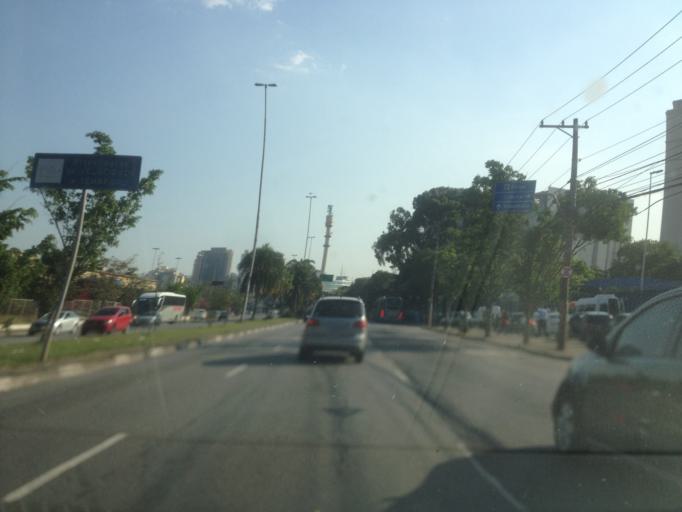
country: BR
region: Sao Paulo
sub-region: Sao Paulo
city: Sao Paulo
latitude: -23.5206
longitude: -46.6578
